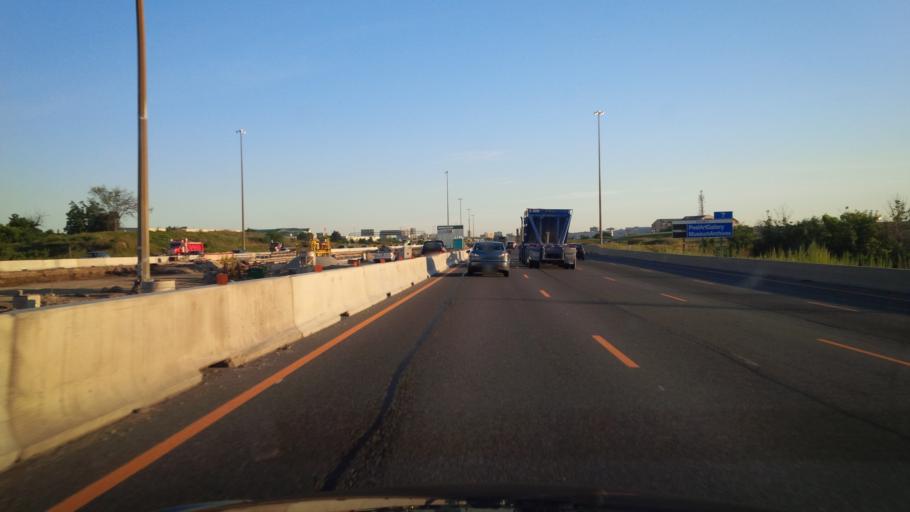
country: CA
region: Ontario
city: Brampton
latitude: 43.6728
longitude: -79.7033
